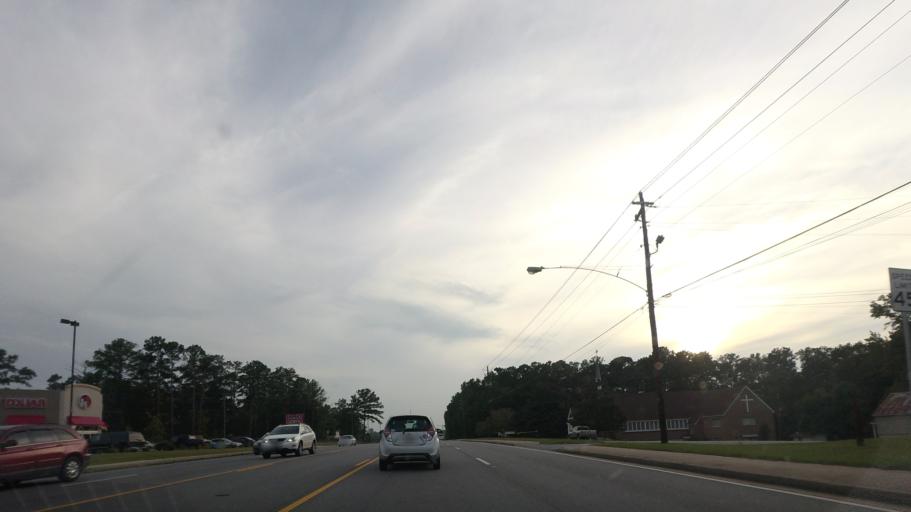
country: US
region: Georgia
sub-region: Bibb County
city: Macon
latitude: 32.8639
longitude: -83.5885
